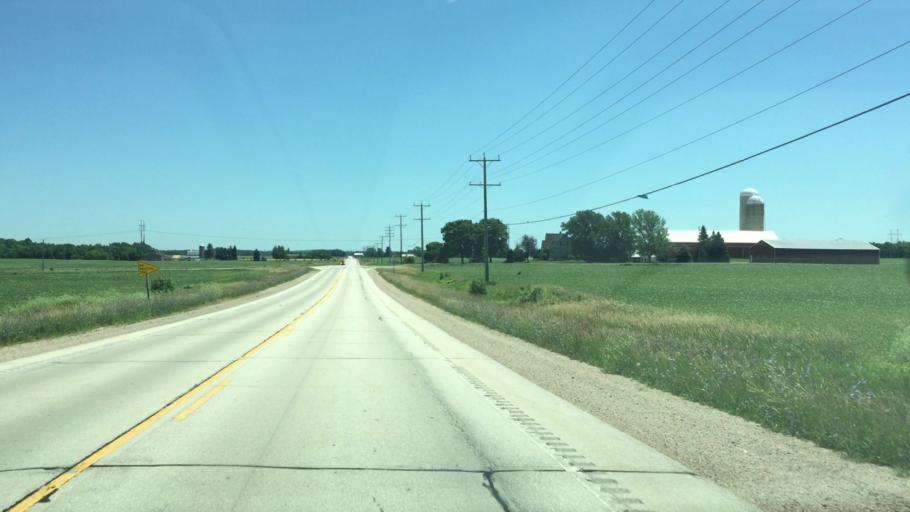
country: US
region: Wisconsin
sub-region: Calumet County
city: Sherwood
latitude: 44.1406
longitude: -88.2274
